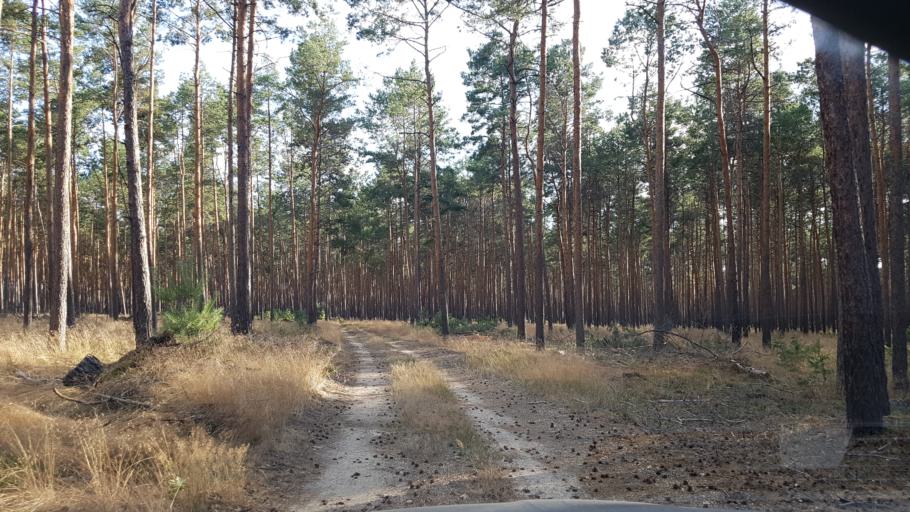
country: DE
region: Brandenburg
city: Trobitz
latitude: 51.6231
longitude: 13.4101
